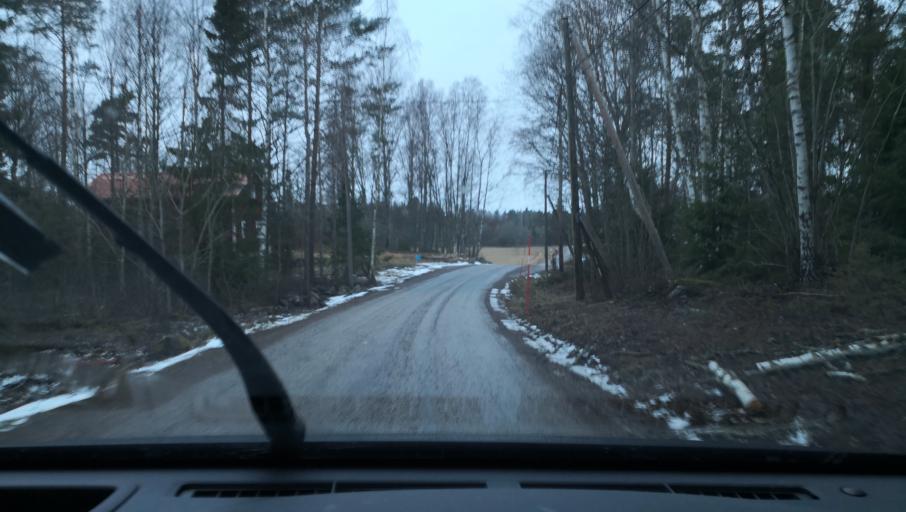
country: SE
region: Uppsala
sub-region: Enkopings Kommun
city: Hummelsta
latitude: 59.4570
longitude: 16.8507
